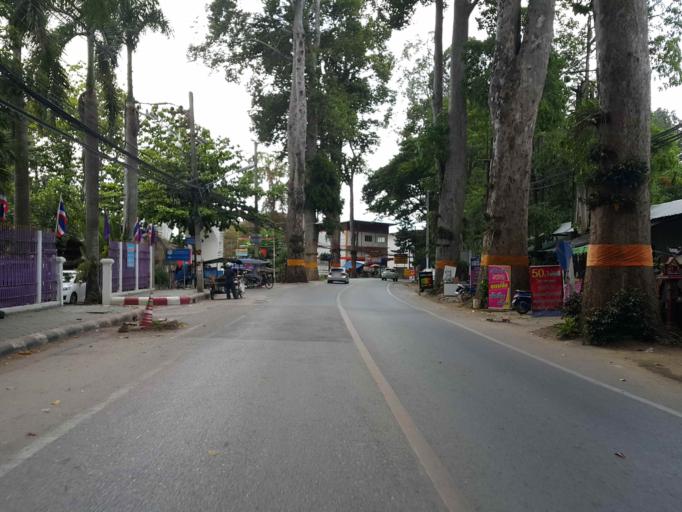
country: TH
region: Chiang Mai
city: Saraphi
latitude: 18.7174
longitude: 99.0296
